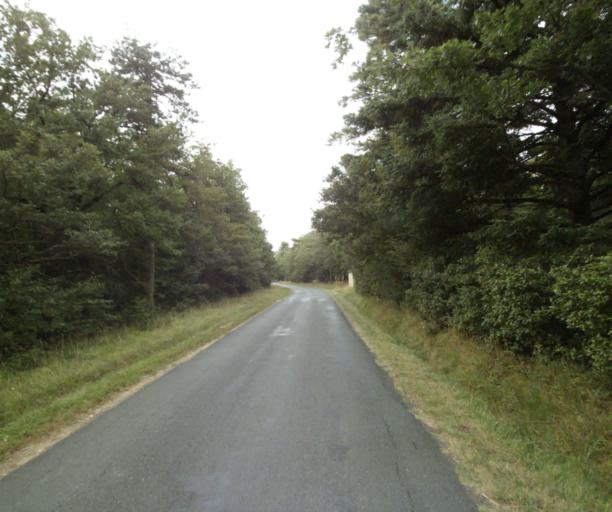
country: FR
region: Midi-Pyrenees
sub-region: Departement du Tarn
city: Soreze
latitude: 43.4664
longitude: 2.0826
